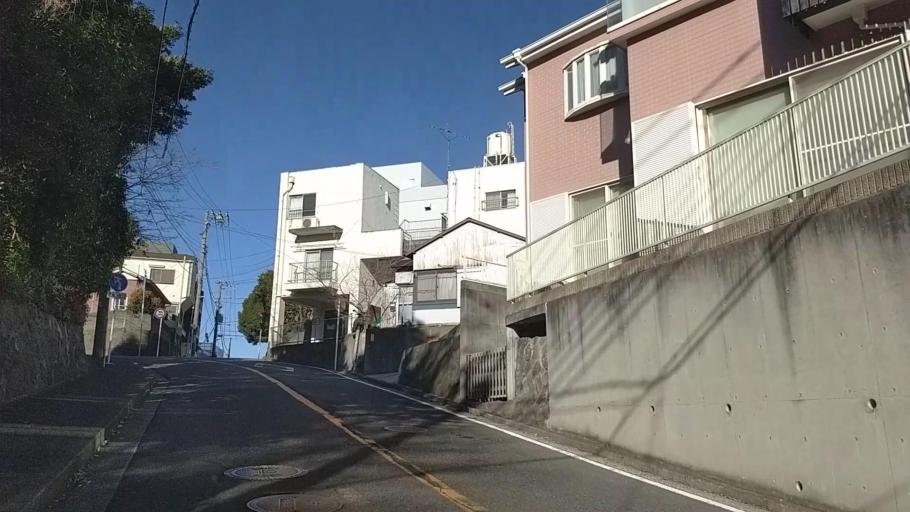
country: JP
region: Kanagawa
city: Yokohama
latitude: 35.4725
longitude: 139.6268
